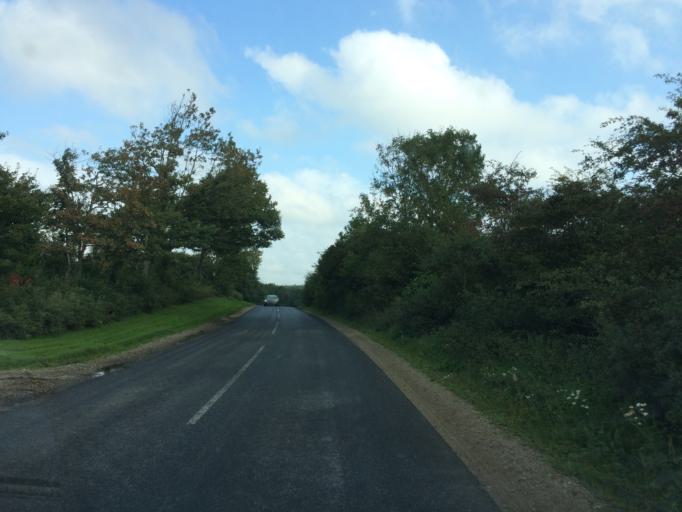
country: DK
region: Central Jutland
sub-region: Holstebro Kommune
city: Vinderup
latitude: 56.4603
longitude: 8.8795
